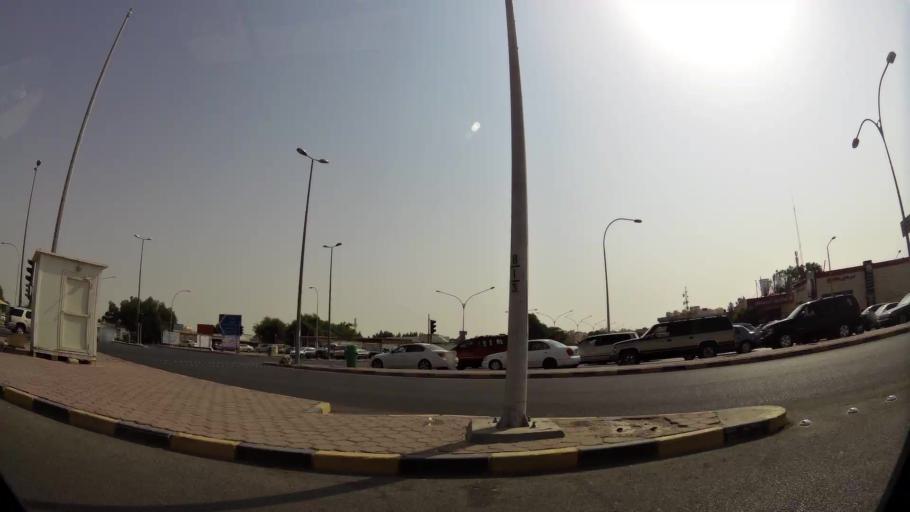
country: KW
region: Muhafazat al Jahra'
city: Al Jahra'
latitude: 29.3291
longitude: 47.6814
